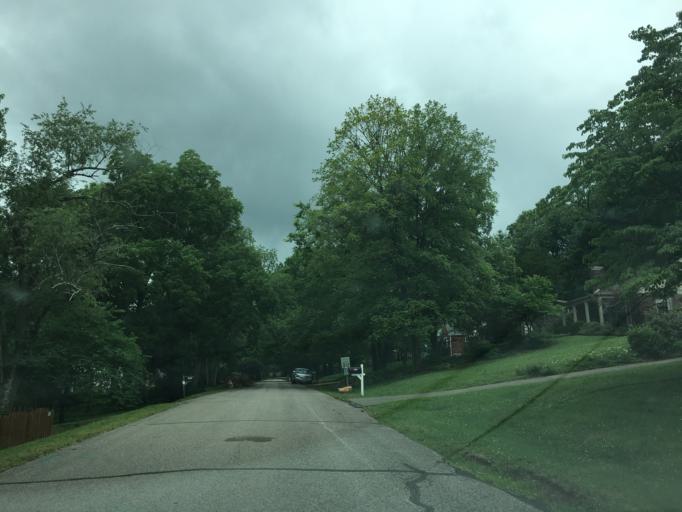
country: US
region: Tennessee
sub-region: Davidson County
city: Oak Hill
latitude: 36.1096
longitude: -86.7792
